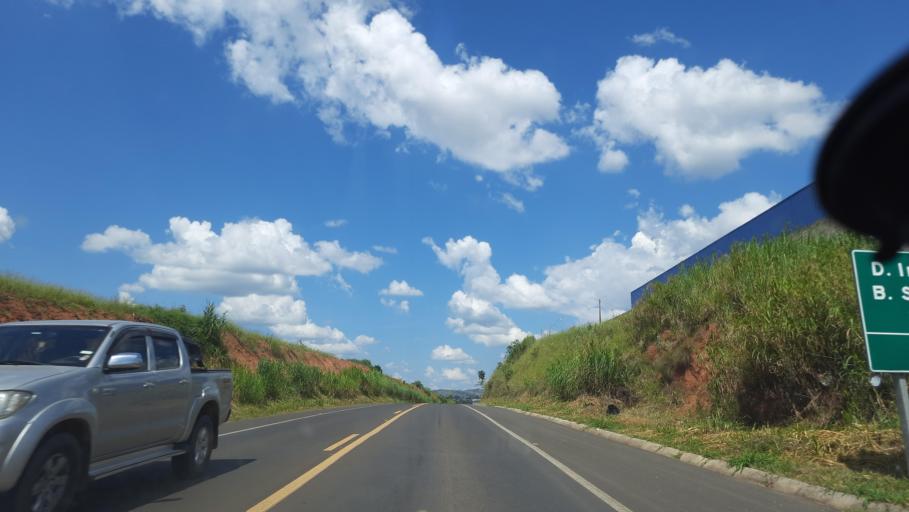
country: BR
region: Sao Paulo
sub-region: Sao Jose Do Rio Pardo
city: Sao Jose do Rio Pardo
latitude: -21.6033
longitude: -46.9212
